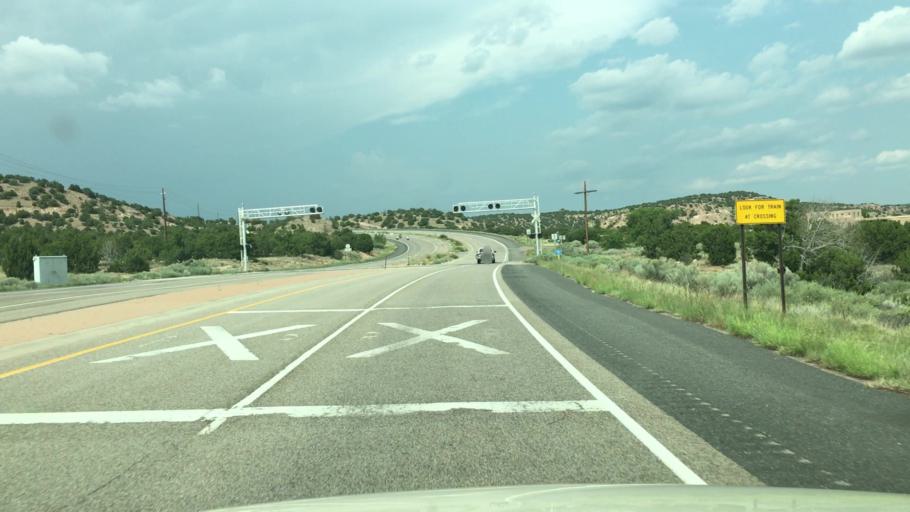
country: US
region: New Mexico
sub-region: Santa Fe County
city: Eldorado at Santa Fe
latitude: 35.4840
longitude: -105.9062
